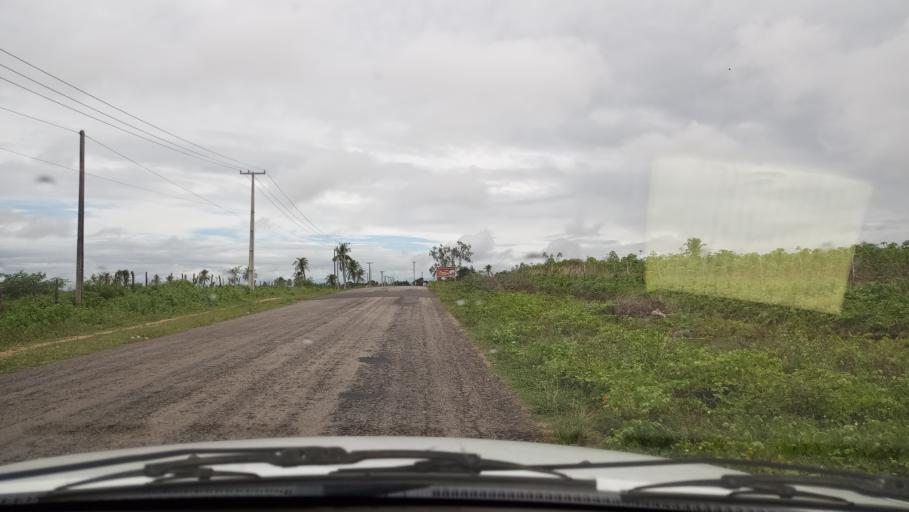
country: BR
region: Rio Grande do Norte
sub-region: Poco Branco
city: Poco Branco
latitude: -5.6150
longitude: -35.6494
